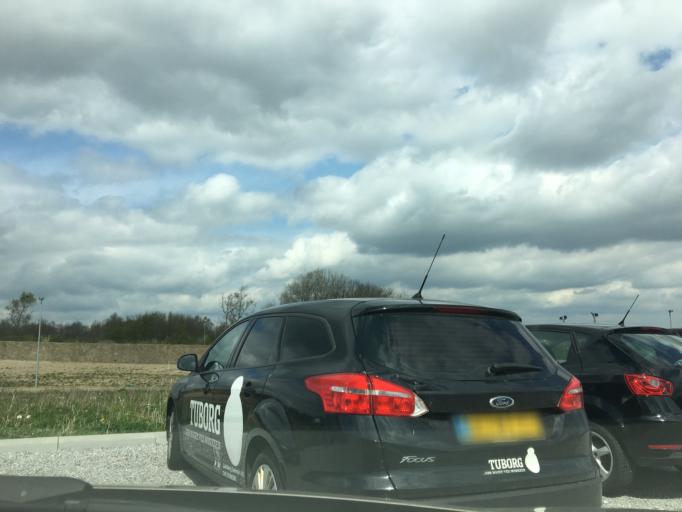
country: DK
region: Central Jutland
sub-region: Skanderborg Kommune
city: Skanderborg
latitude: 56.0485
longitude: 9.9323
